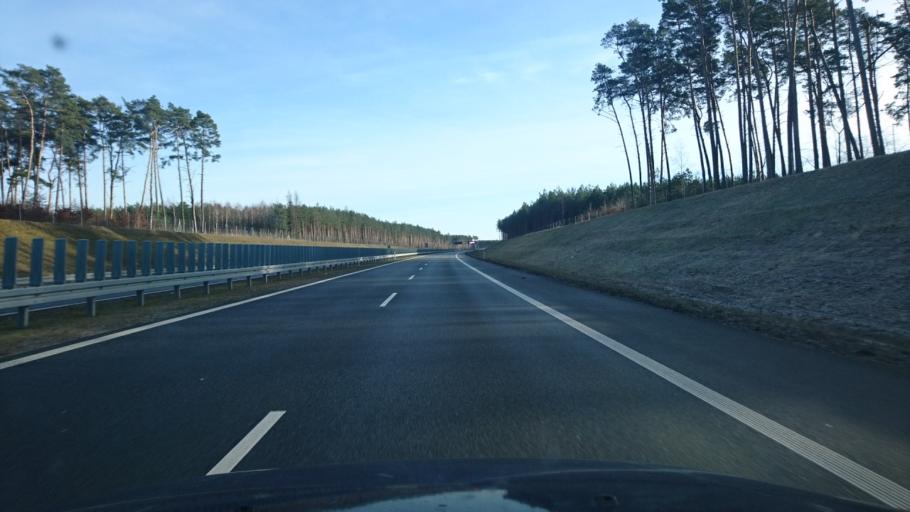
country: PL
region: Greater Poland Voivodeship
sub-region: Powiat kepinski
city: Kepno
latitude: 51.3298
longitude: 17.9751
